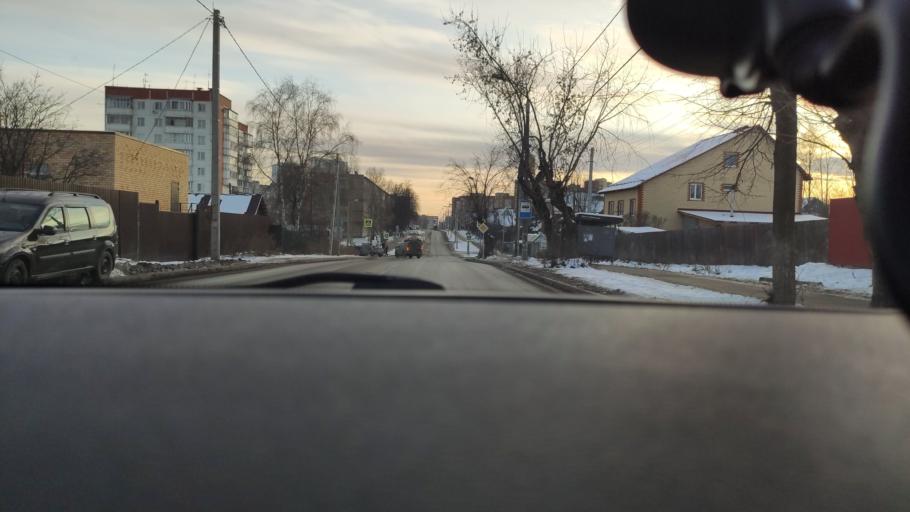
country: RU
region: Perm
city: Perm
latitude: 58.1085
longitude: 56.2968
